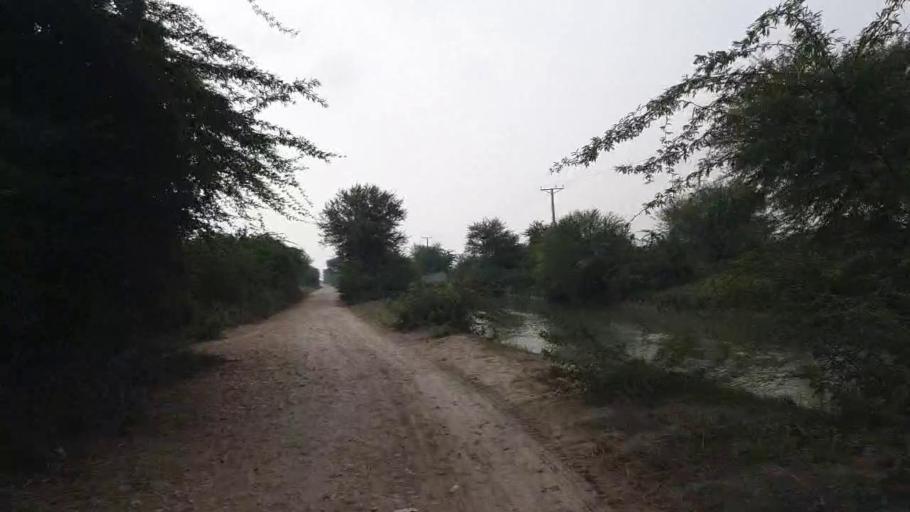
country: PK
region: Sindh
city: Kario
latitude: 24.8694
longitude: 68.5177
